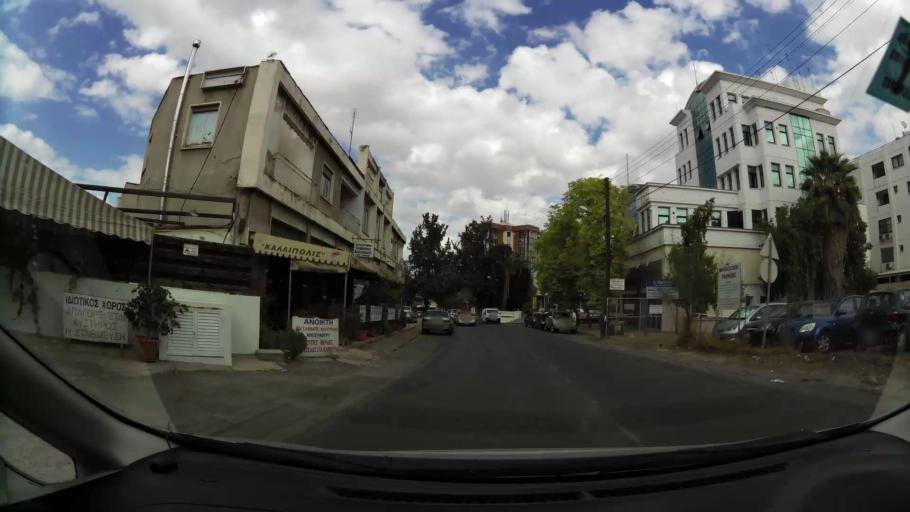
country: CY
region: Lefkosia
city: Nicosia
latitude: 35.1662
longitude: 33.3711
